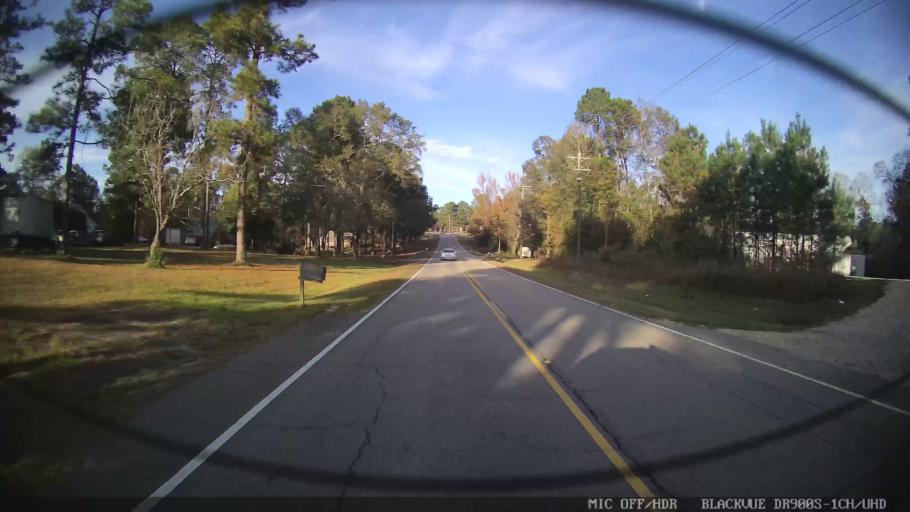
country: US
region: Mississippi
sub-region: Lamar County
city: Purvis
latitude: 31.1883
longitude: -89.2889
